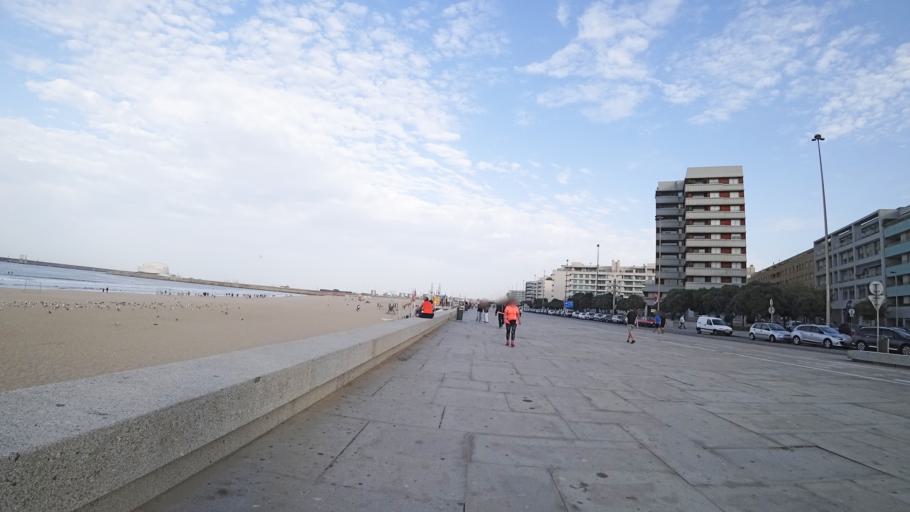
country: PT
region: Porto
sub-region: Matosinhos
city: Matosinhos
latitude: 41.1747
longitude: -8.6901
